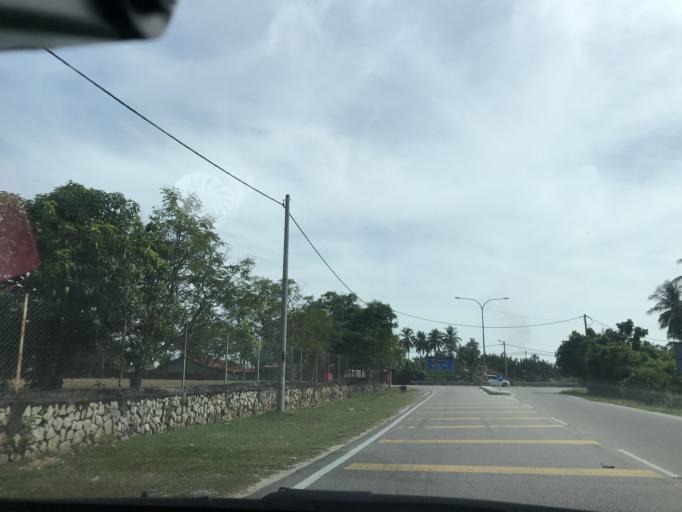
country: MY
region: Kelantan
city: Tumpat
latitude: 6.2013
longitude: 102.1563
